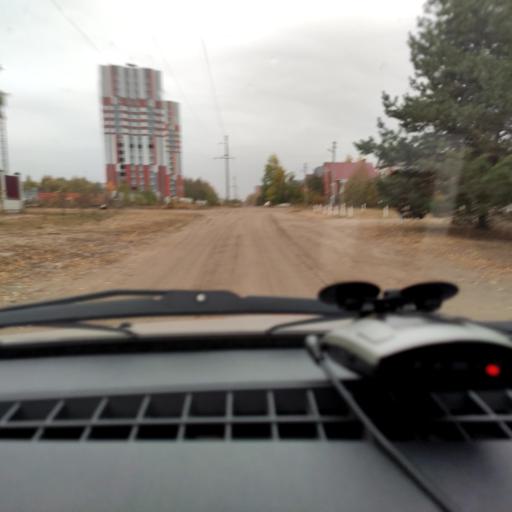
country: RU
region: Voronezj
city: Podgornoye
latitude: 51.7620
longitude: 39.1777
